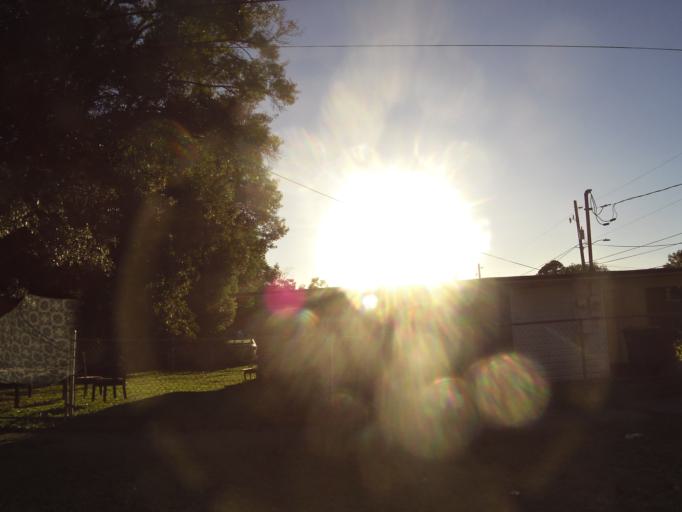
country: US
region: Florida
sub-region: Duval County
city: Jacksonville
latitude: 30.3609
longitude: -81.7023
